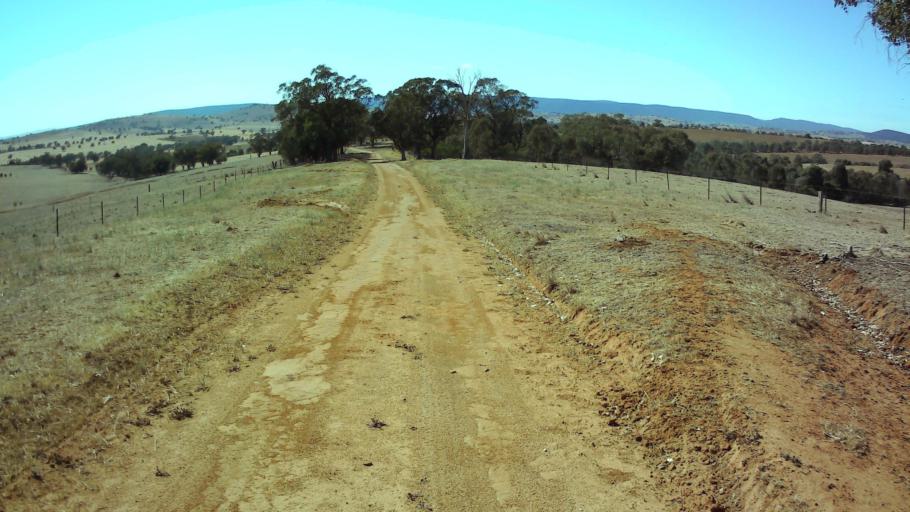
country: AU
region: New South Wales
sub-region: Cowra
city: Cowra
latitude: -33.9776
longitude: 148.4663
